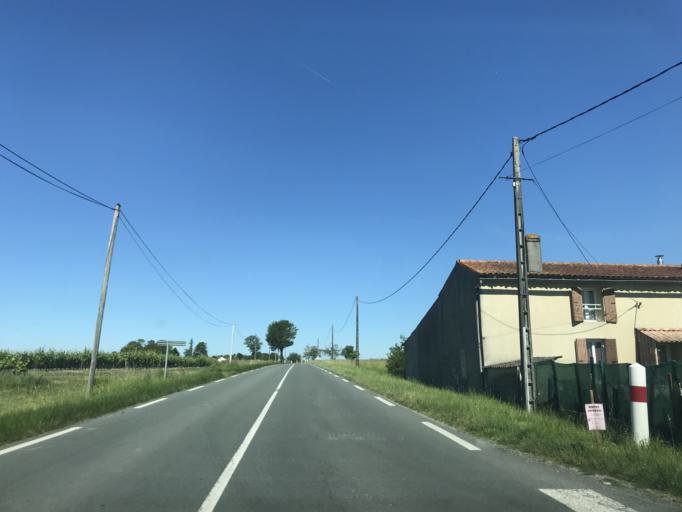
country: FR
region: Poitou-Charentes
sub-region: Departement de la Charente-Maritime
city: Perignac
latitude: 45.5719
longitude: -0.4140
